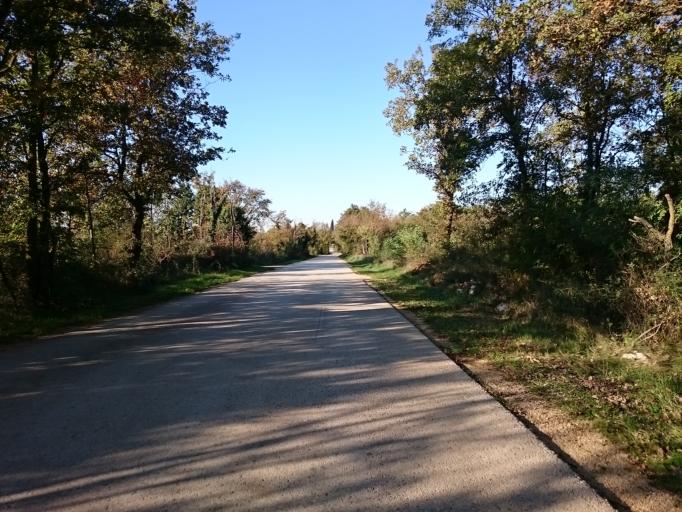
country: HR
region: Istarska
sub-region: Grad Porec
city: Porec
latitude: 45.2848
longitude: 13.6432
